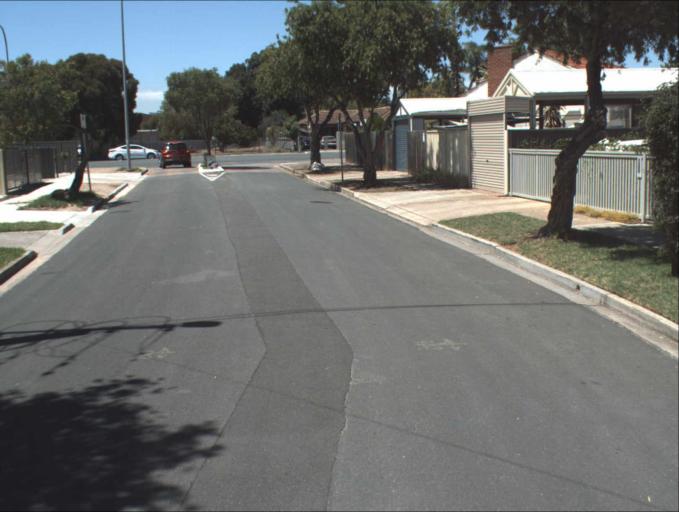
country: AU
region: South Australia
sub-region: Port Adelaide Enfield
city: Klemzig
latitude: -34.8710
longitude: 138.6183
